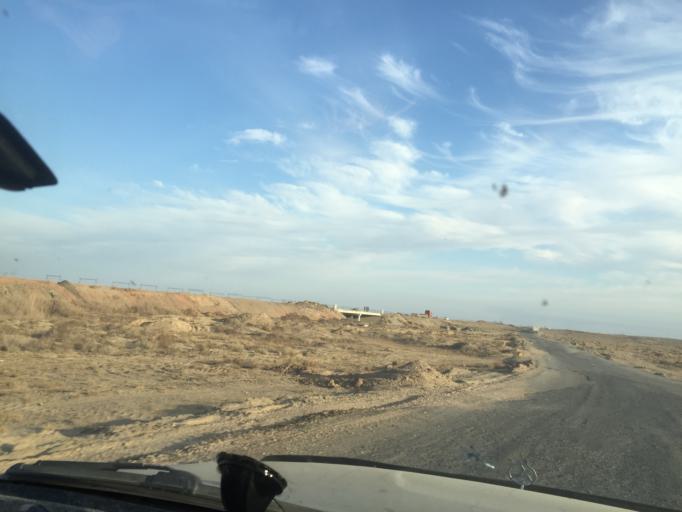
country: KZ
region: Almaty Oblysy
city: Ulken
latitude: 45.2444
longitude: 73.8202
